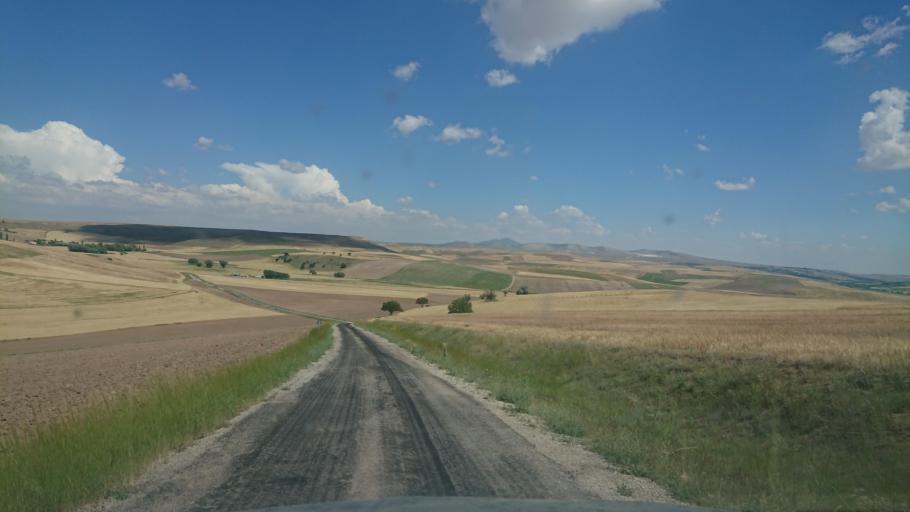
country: TR
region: Aksaray
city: Agacoren
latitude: 38.8013
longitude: 33.8151
